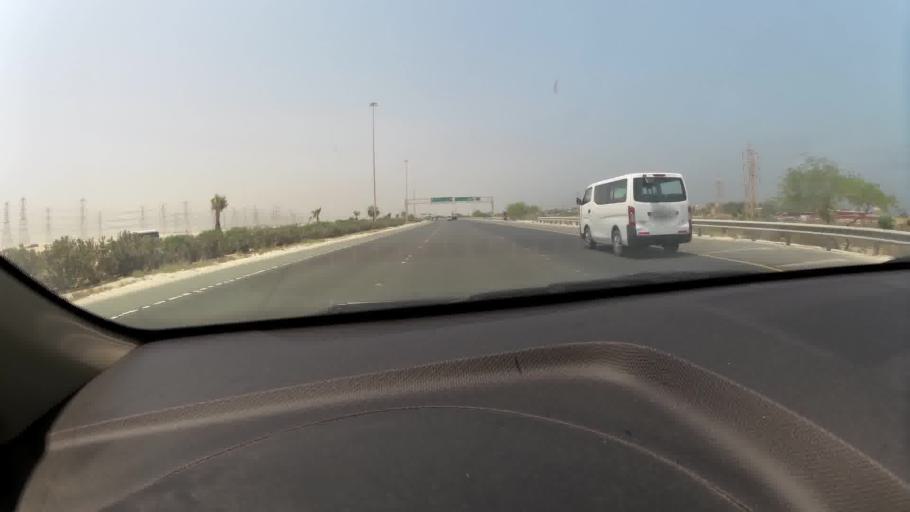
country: KW
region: Al Ahmadi
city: Al Fahahil
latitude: 28.9092
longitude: 48.2144
